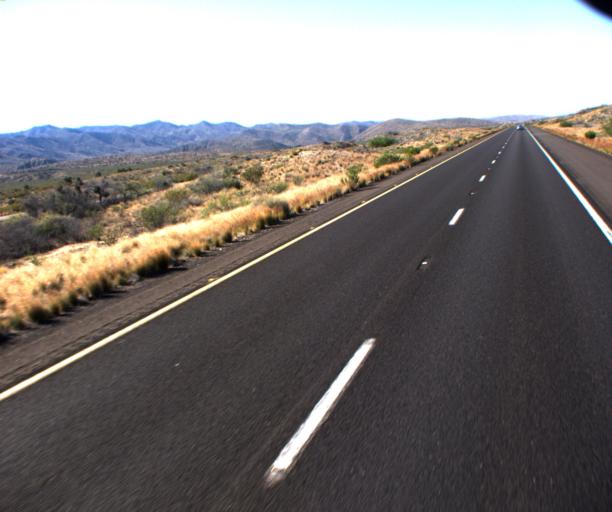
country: US
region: Arizona
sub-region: Mohave County
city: Kingman
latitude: 35.0517
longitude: -113.6654
